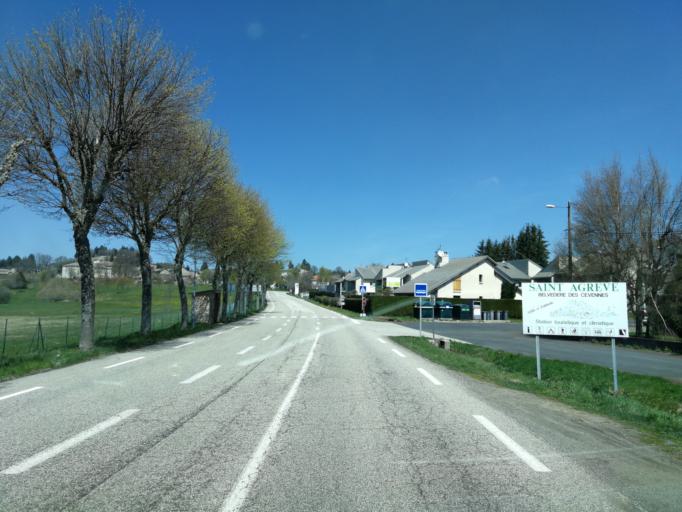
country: FR
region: Rhone-Alpes
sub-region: Departement de l'Ardeche
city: Saint-Agreve
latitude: 45.0034
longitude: 4.4032
